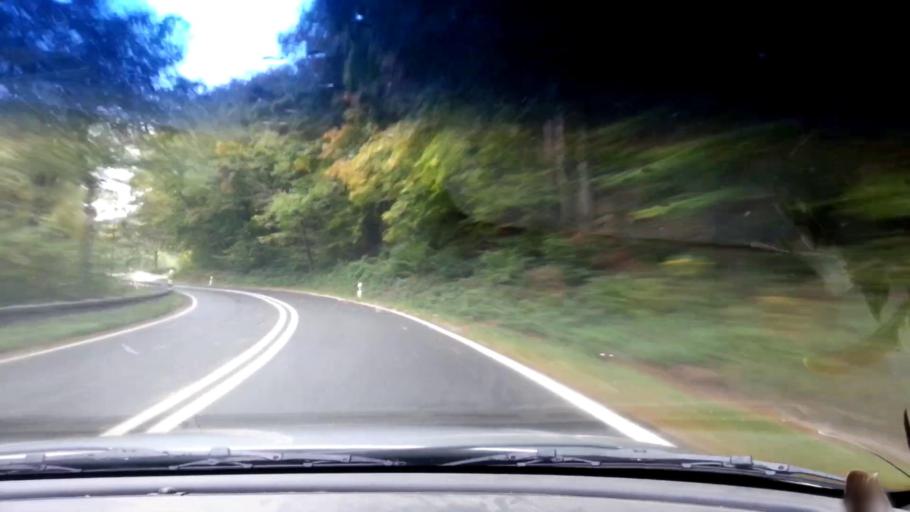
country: DE
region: Bavaria
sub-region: Upper Franconia
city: Poxdorf
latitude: 49.9780
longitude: 11.1000
